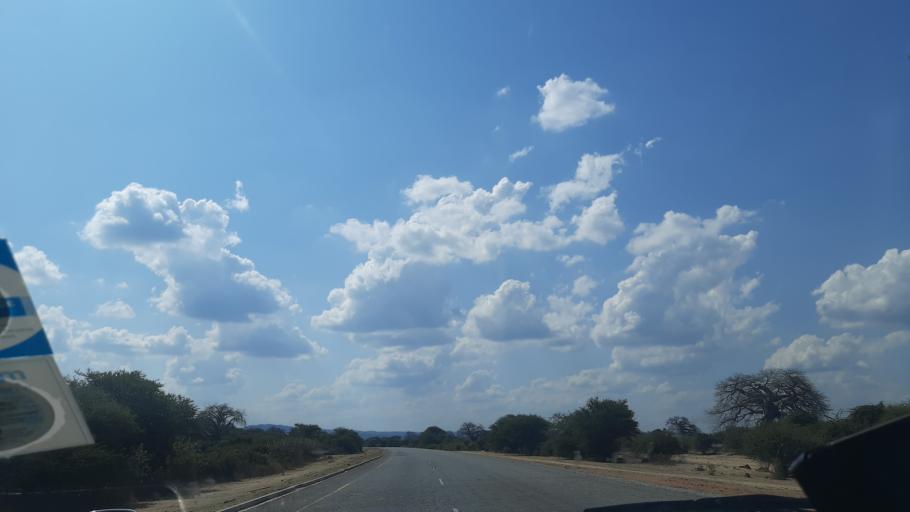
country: TZ
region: Singida
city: Kilimatinde
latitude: -5.8387
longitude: 35.0646
